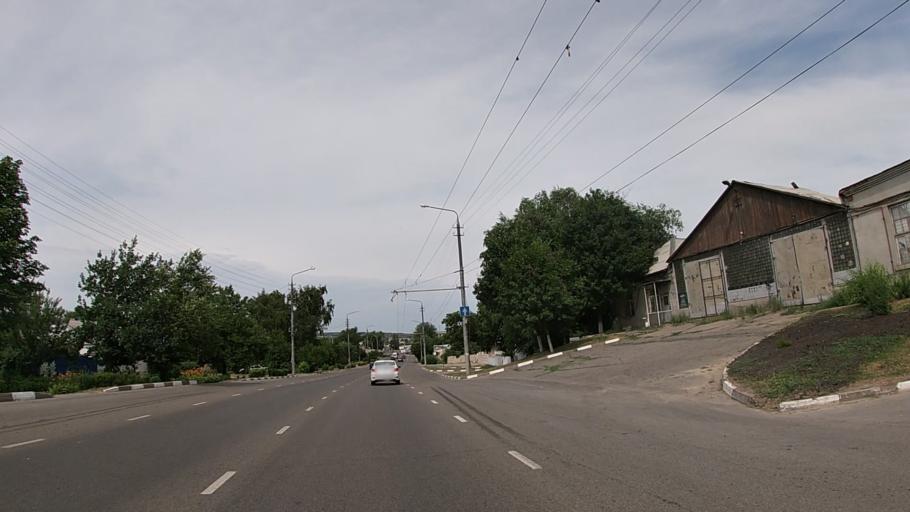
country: RU
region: Belgorod
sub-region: Belgorodskiy Rayon
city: Belgorod
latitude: 50.6017
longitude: 36.5664
